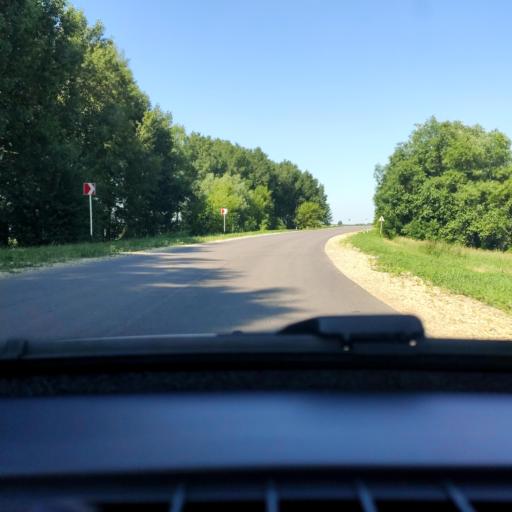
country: RU
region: Voronezj
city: Anna
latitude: 51.6471
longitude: 40.3667
